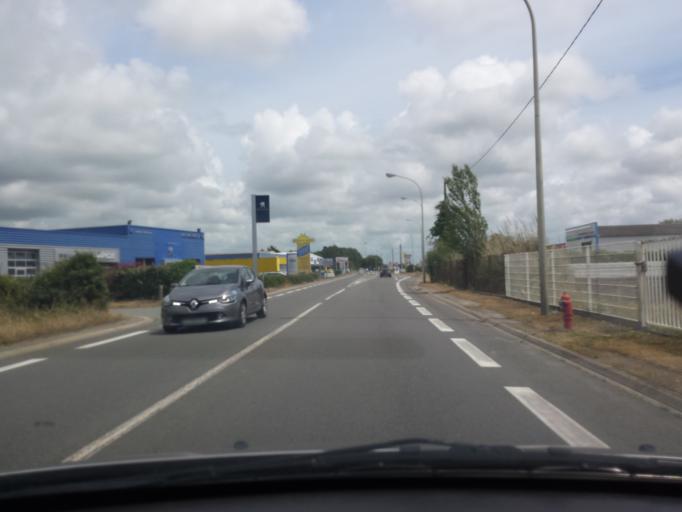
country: FR
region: Pays de la Loire
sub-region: Departement de la Vendee
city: Le Fenouiller
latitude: 46.6938
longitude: -1.9030
